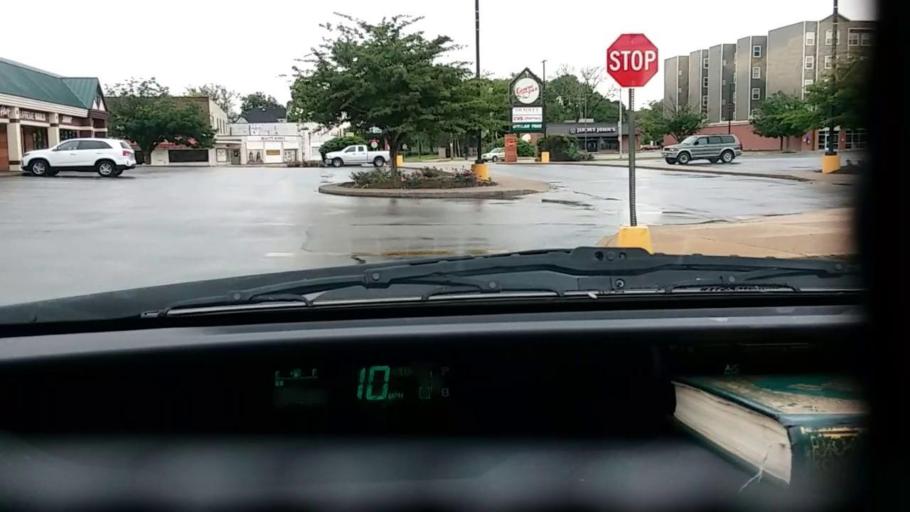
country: US
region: Illinois
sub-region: Peoria County
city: West Peoria
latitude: 40.6989
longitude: -89.6119
